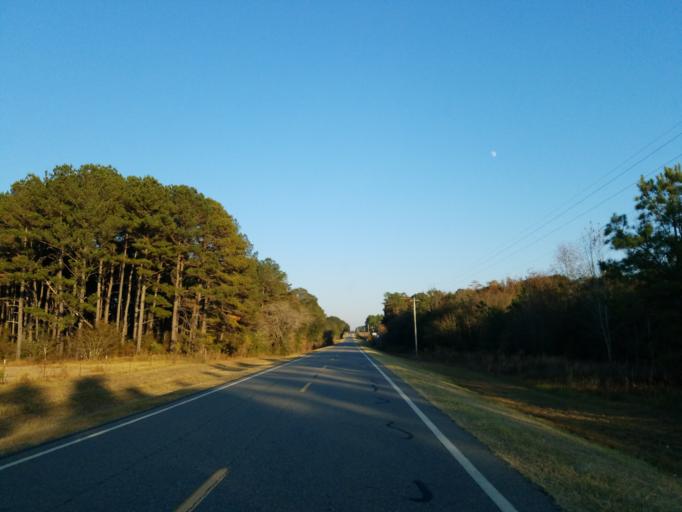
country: US
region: Georgia
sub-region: Turner County
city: Ashburn
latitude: 31.8596
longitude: -83.6360
